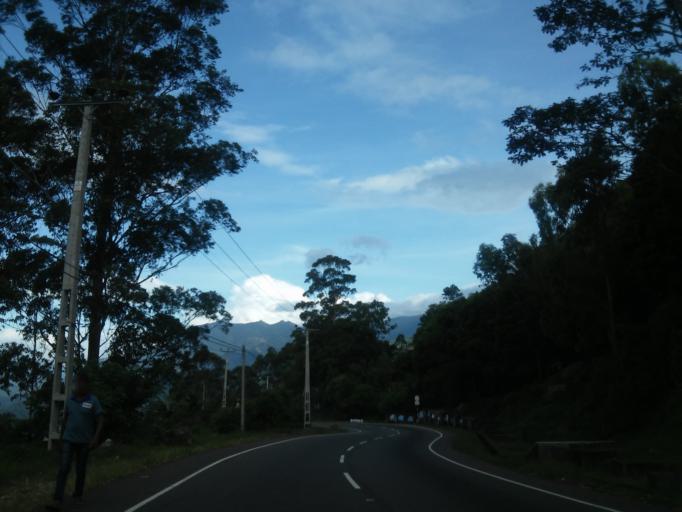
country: LK
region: Uva
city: Haputale
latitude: 6.7627
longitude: 80.9230
